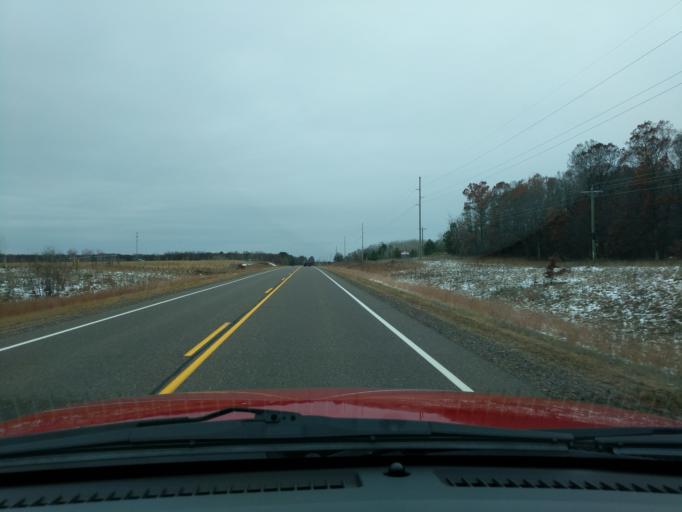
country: US
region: Wisconsin
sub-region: Washburn County
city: Shell Lake
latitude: 45.8158
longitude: -92.1176
